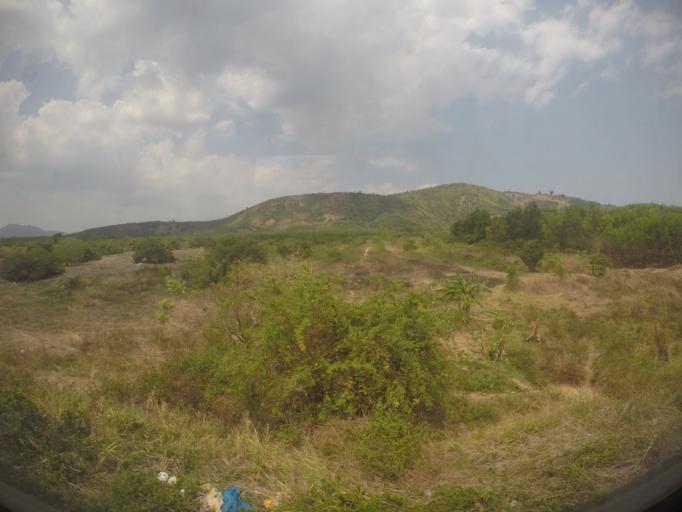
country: VN
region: Binh Thuan
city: Tanh Linh
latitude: 10.9123
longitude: 107.6805
